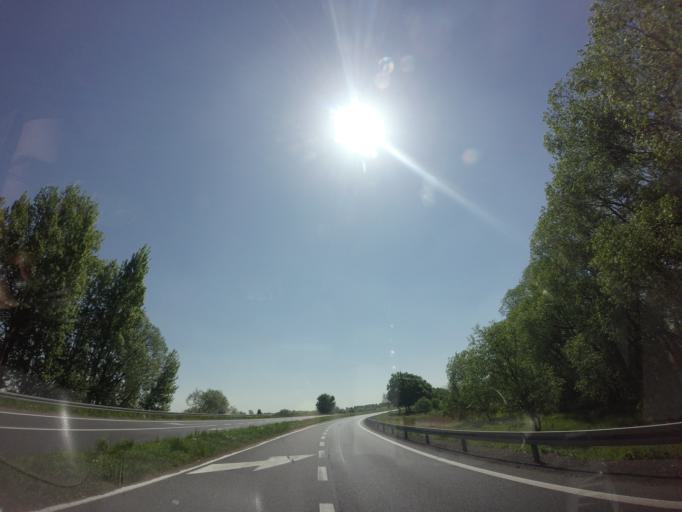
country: PL
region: West Pomeranian Voivodeship
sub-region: Powiat pyrzycki
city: Lipiany
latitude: 52.9888
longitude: 14.9793
